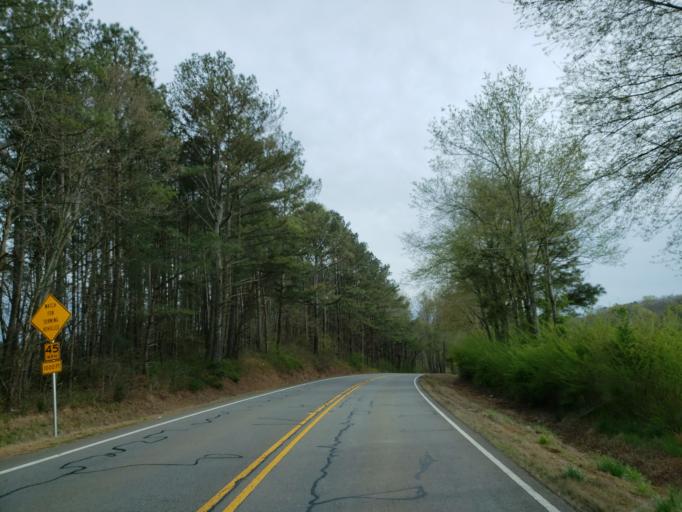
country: US
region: Georgia
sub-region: Pickens County
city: Nelson
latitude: 34.3924
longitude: -84.4330
